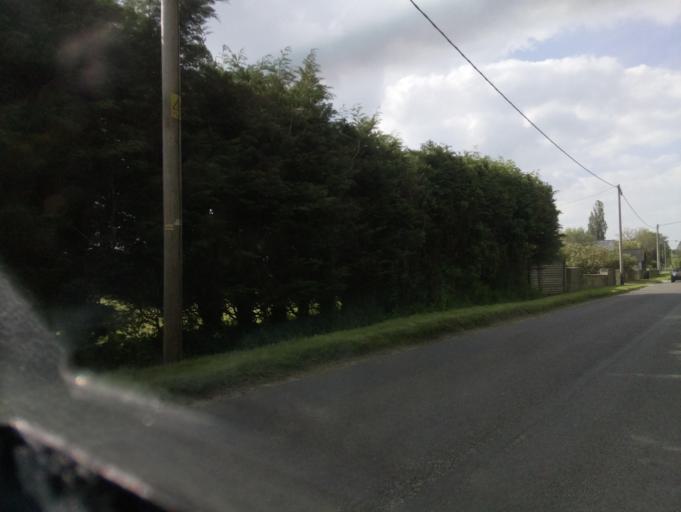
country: GB
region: England
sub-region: Wiltshire
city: Malmesbury
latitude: 51.5361
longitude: -2.0798
